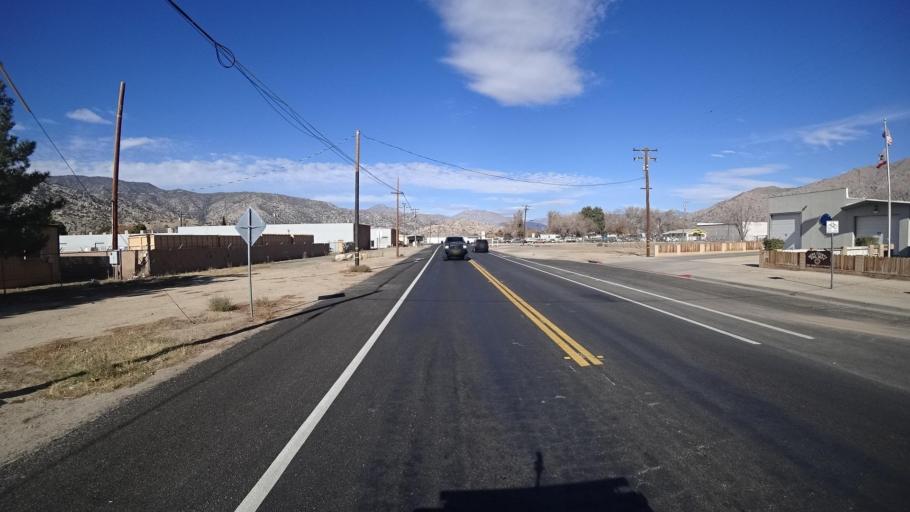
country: US
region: California
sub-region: Kern County
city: Bodfish
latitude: 35.6037
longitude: -118.4861
